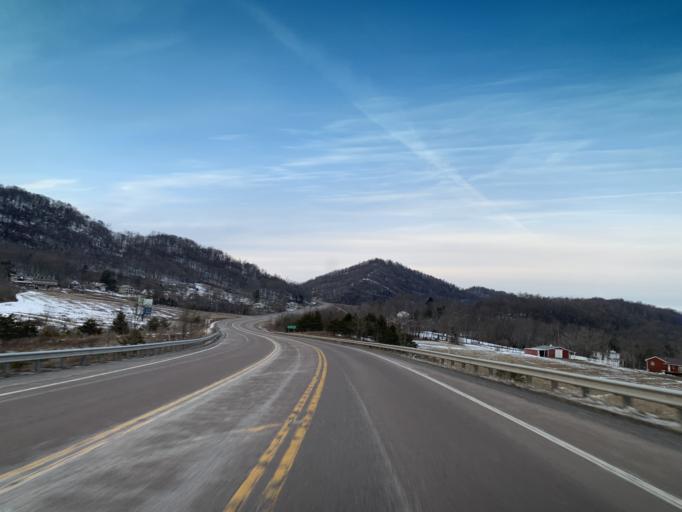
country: US
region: Maryland
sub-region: Allegany County
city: Cumberland
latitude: 39.7110
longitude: -78.7017
